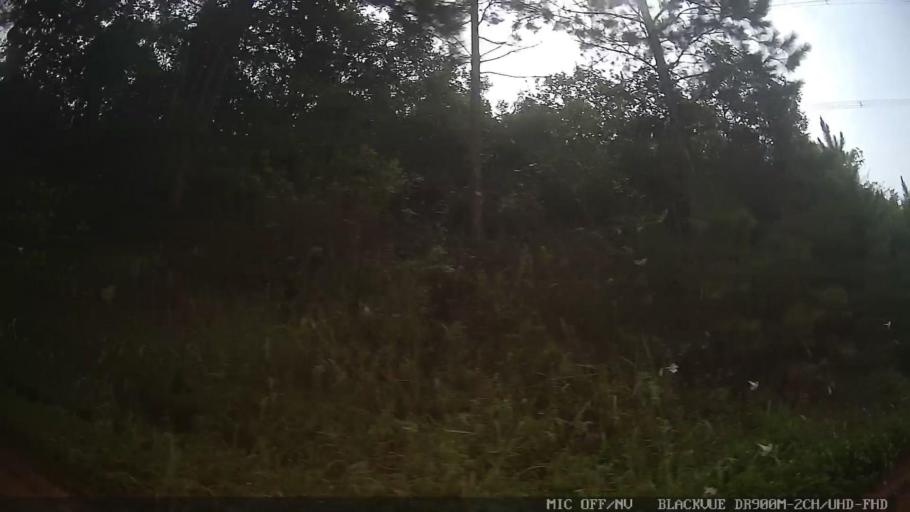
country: BR
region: Sao Paulo
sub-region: Suzano
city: Suzano
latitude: -23.6543
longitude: -46.2596
